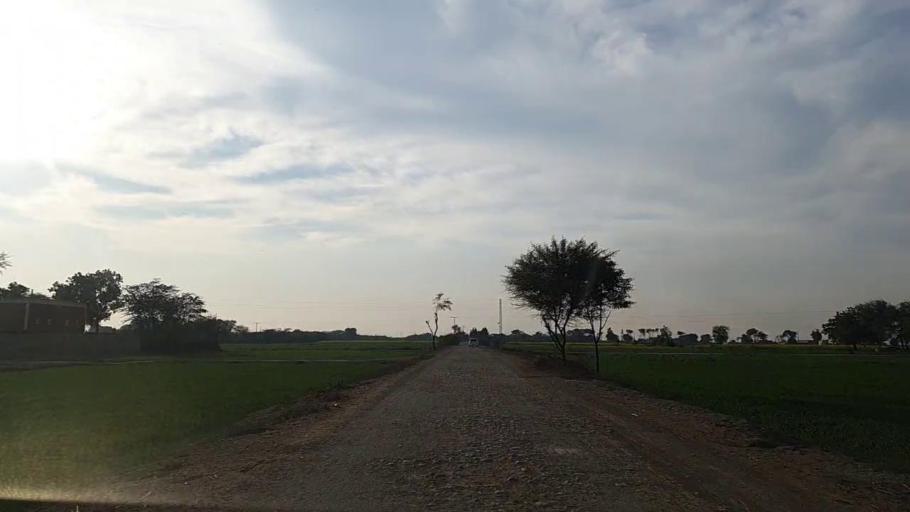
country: PK
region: Sindh
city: Bandhi
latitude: 26.5647
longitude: 68.2645
